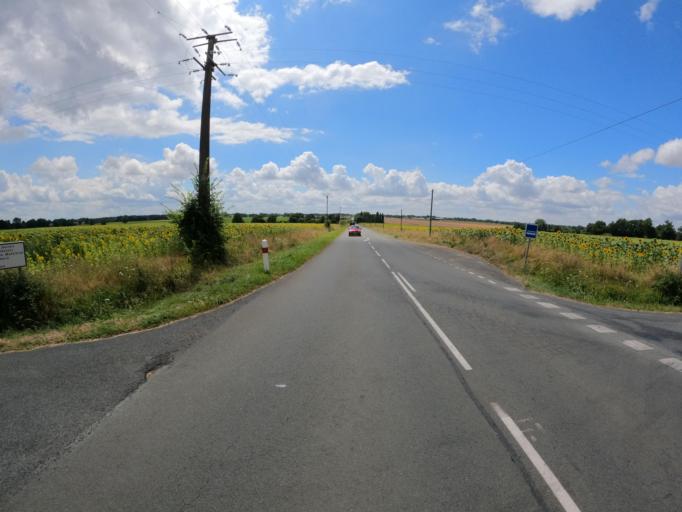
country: FR
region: Pays de la Loire
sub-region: Departement de Maine-et-Loire
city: Chateauneuf-sur-Sarthe
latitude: 47.7114
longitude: -0.5328
